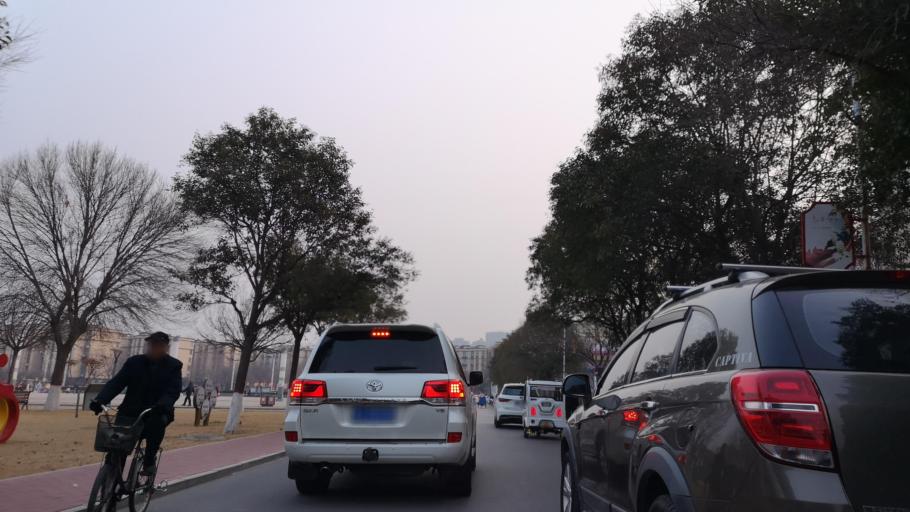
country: CN
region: Henan Sheng
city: Zhongyuanlu
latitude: 35.7853
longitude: 115.0784
